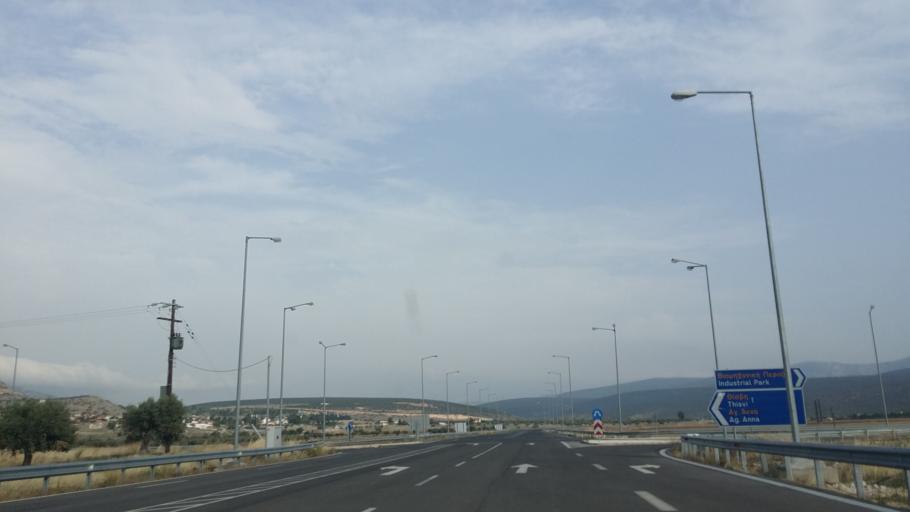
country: GR
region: Central Greece
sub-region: Nomos Voiotias
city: Korini
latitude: 38.2484
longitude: 22.9667
